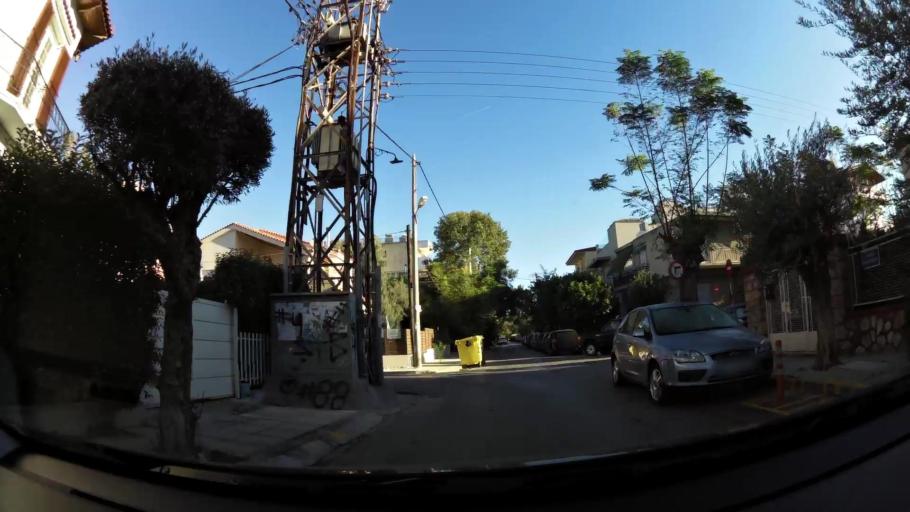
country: GR
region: Attica
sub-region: Nomarchia Athinas
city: Khalandrion
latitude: 38.0161
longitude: 23.7959
